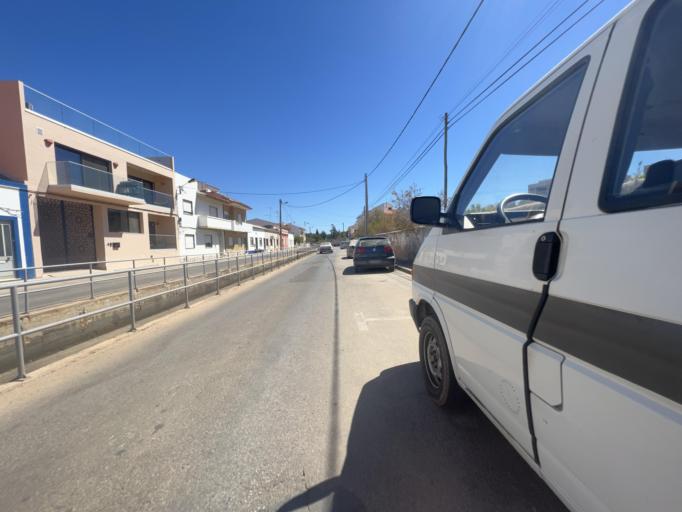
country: PT
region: Faro
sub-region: Portimao
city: Portimao
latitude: 37.1250
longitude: -8.5153
